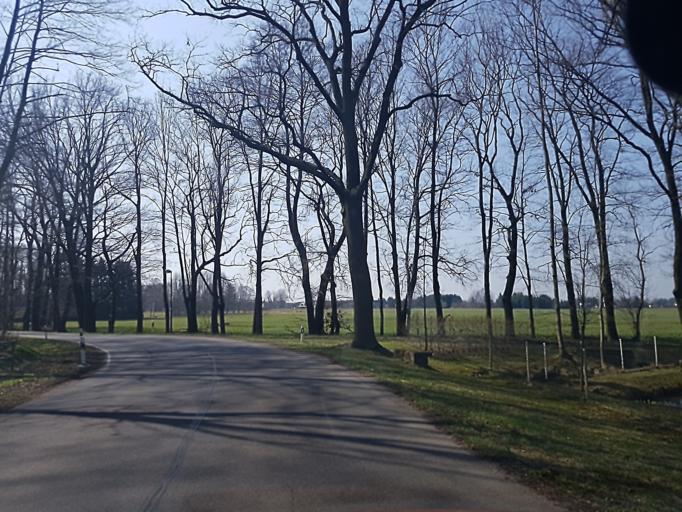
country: DE
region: Brandenburg
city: Forst
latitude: 51.6795
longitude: 14.5406
